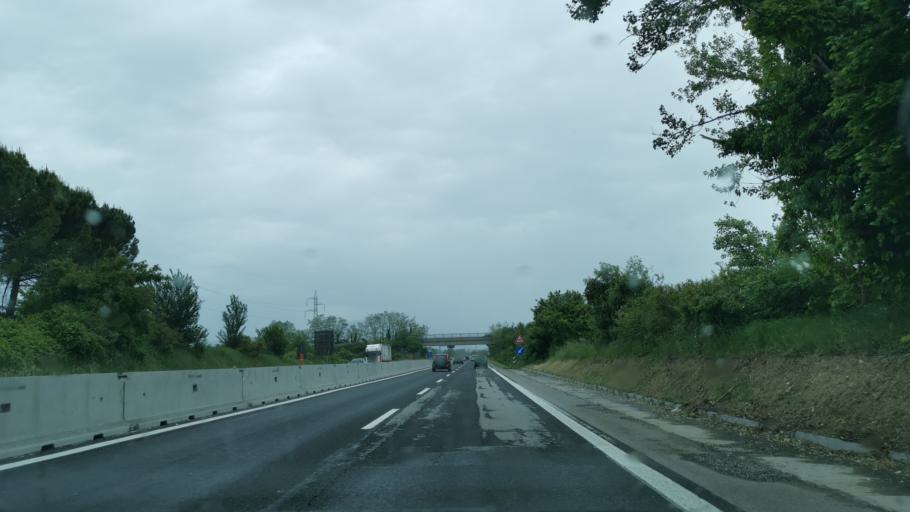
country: IT
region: Veneto
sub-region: Provincia di Verona
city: Castelnuovo del Garda
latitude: 45.4454
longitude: 10.7465
